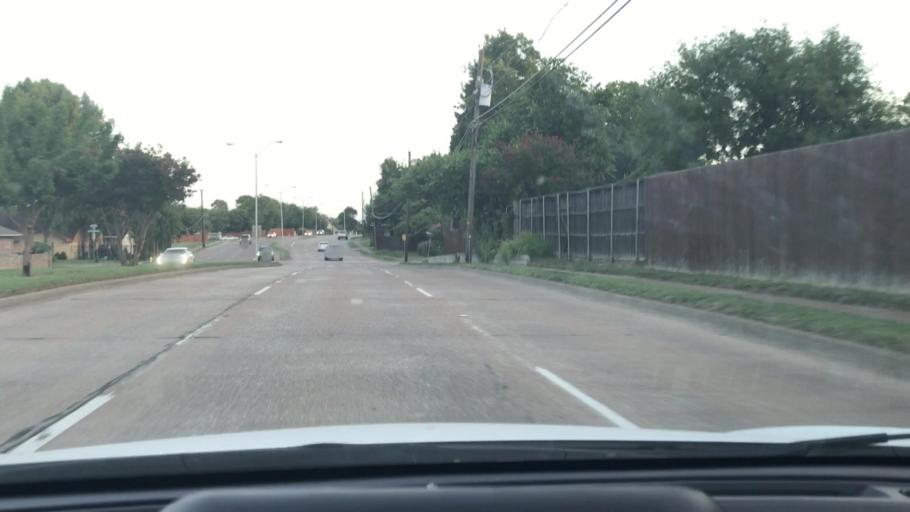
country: US
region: Texas
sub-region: Dallas County
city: Garland
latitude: 32.8766
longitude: -96.7003
